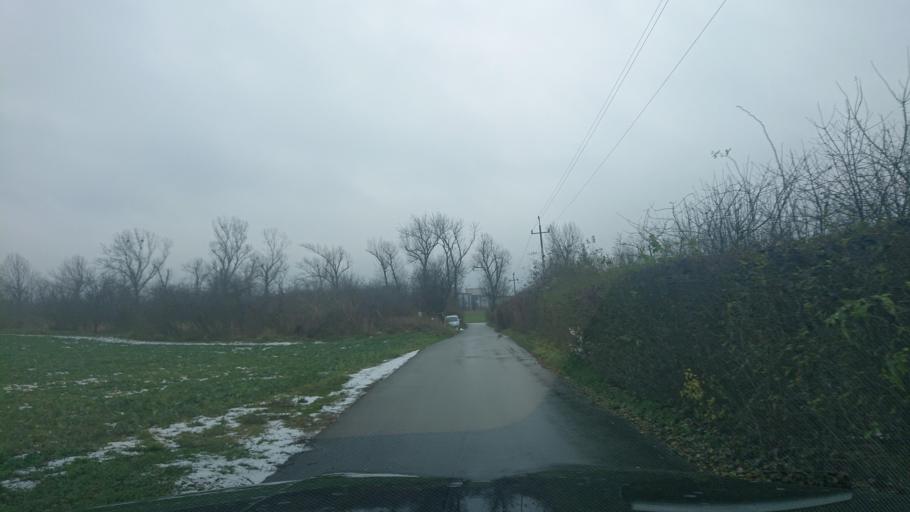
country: PL
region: Greater Poland Voivodeship
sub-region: Powiat gnieznienski
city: Gniezno
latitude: 52.5596
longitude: 17.6041
